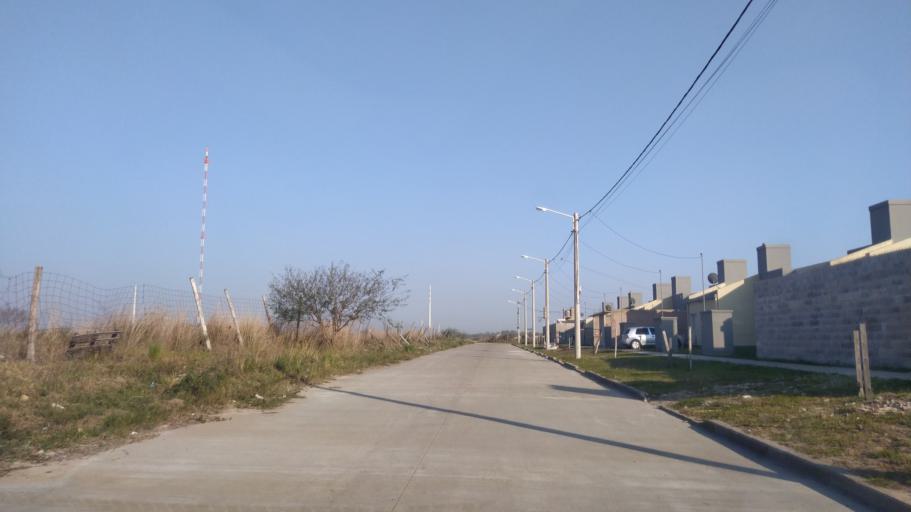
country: AR
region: Corrientes
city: Corrientes
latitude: -27.5281
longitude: -58.8069
